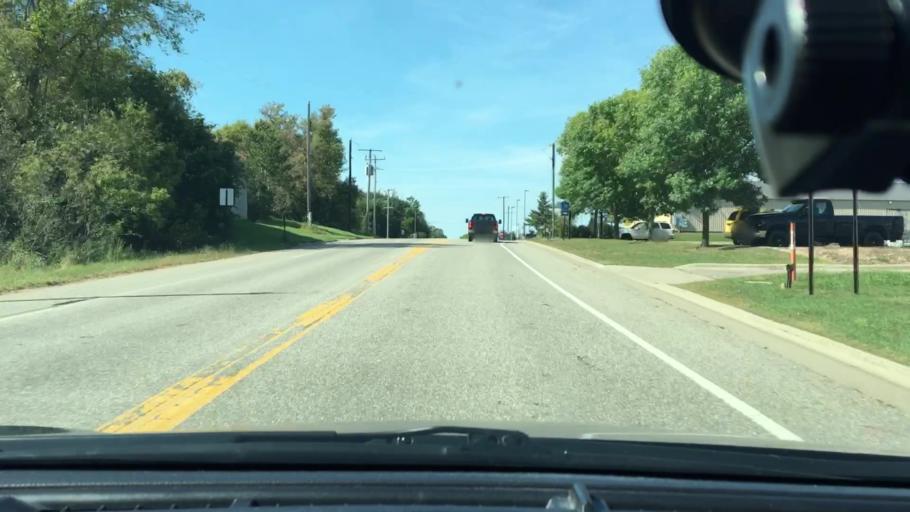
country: US
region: Minnesota
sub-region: Wright County
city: Hanover
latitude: 45.1236
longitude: -93.6329
